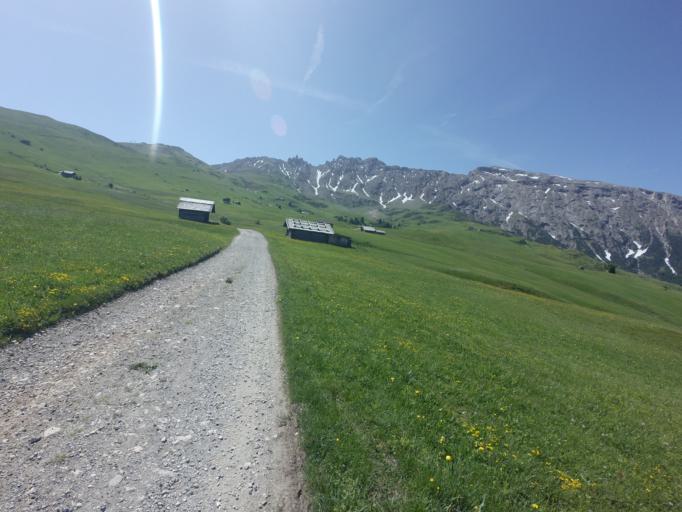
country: IT
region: Trentino-Alto Adige
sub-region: Bolzano
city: Siusi
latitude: 46.5213
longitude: 11.6247
